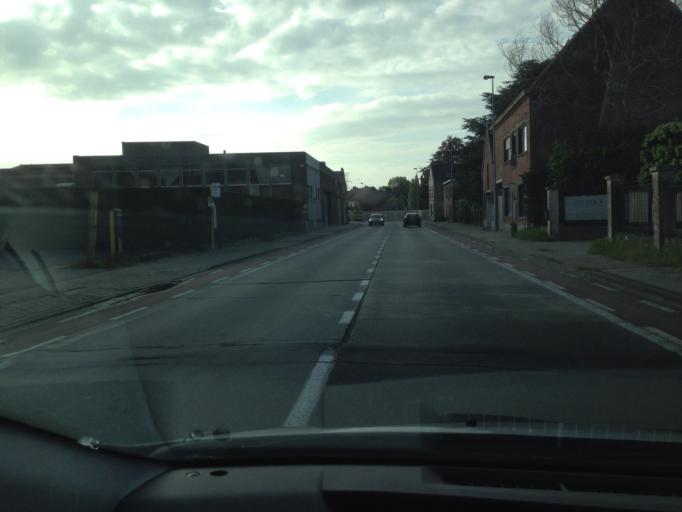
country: BE
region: Flanders
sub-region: Provincie West-Vlaanderen
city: Zedelgem
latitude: 51.1269
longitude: 3.1633
